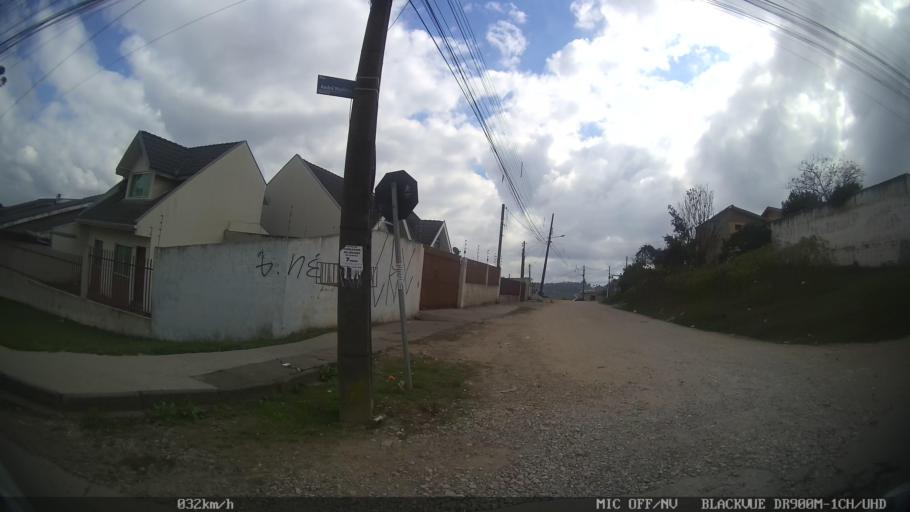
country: BR
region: Parana
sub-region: Colombo
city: Colombo
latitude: -25.3554
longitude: -49.2085
